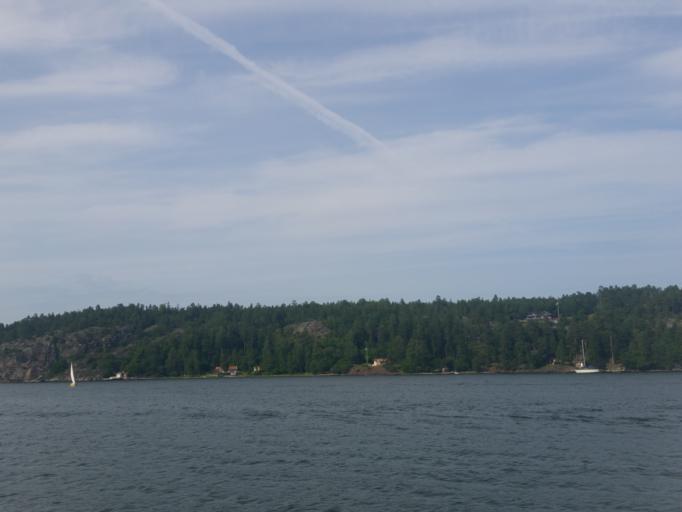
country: SE
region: Stockholm
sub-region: Nacka Kommun
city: Saltsjobaden
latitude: 59.2765
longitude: 18.3338
